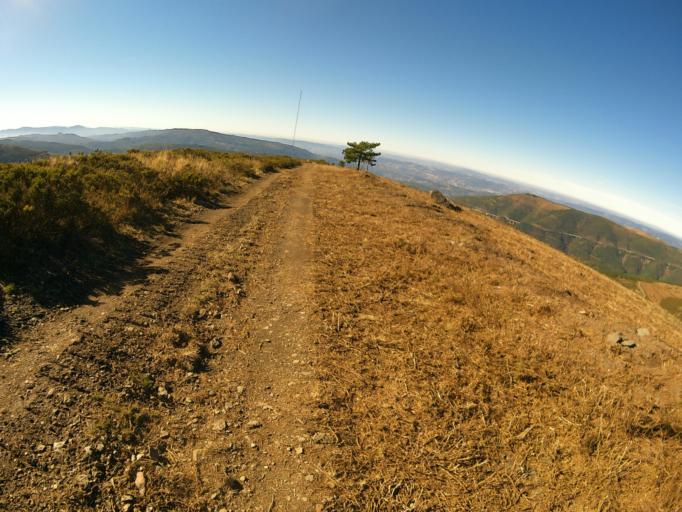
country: PT
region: Vila Real
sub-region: Mesao Frio
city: Mesao Frio
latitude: 41.2502
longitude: -7.9153
